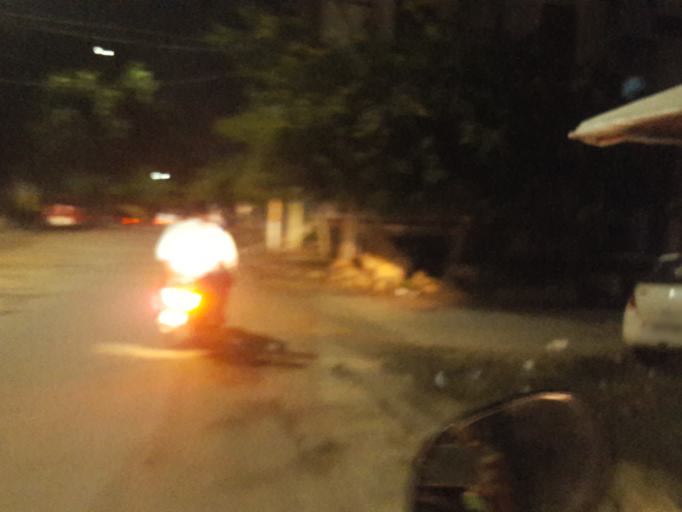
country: IN
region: Telangana
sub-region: Rangareddi
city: Kukatpalli
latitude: 17.4882
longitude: 78.3939
